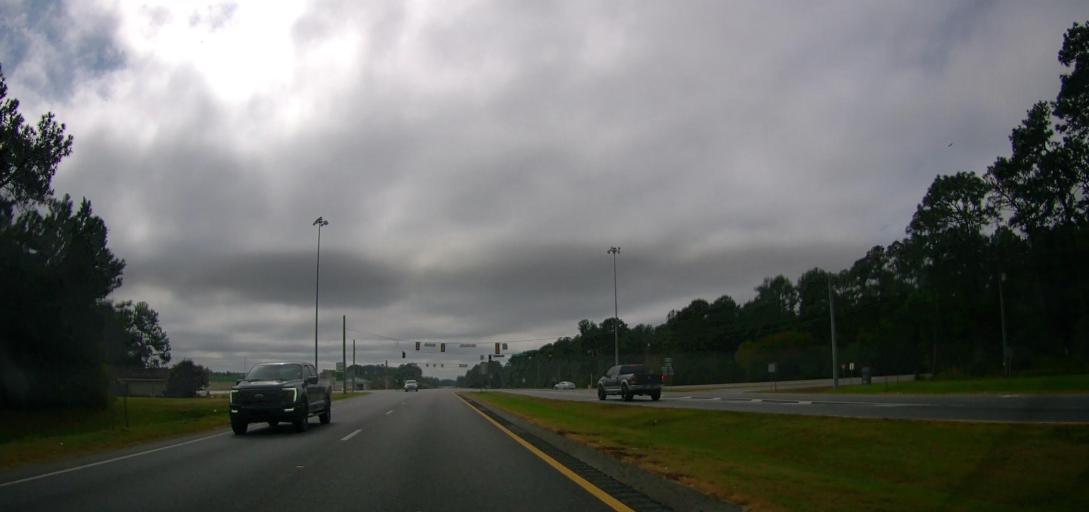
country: US
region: Georgia
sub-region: Colquitt County
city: Moultrie
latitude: 31.1163
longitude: -83.7842
